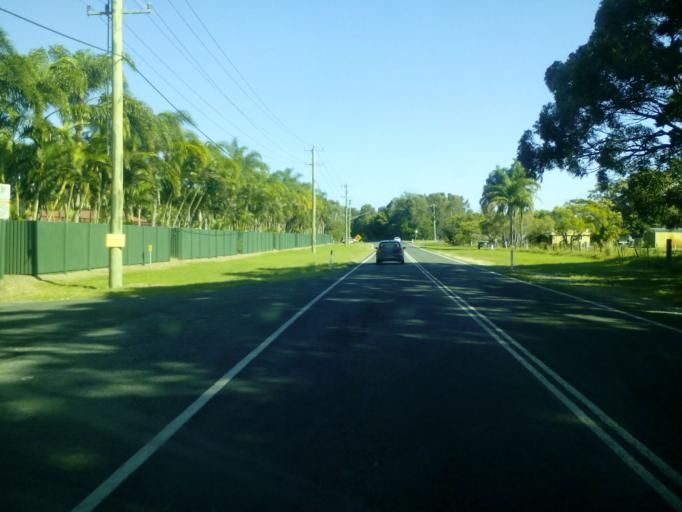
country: AU
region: New South Wales
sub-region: Tweed
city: Kingscliff
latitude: -28.2551
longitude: 153.5597
